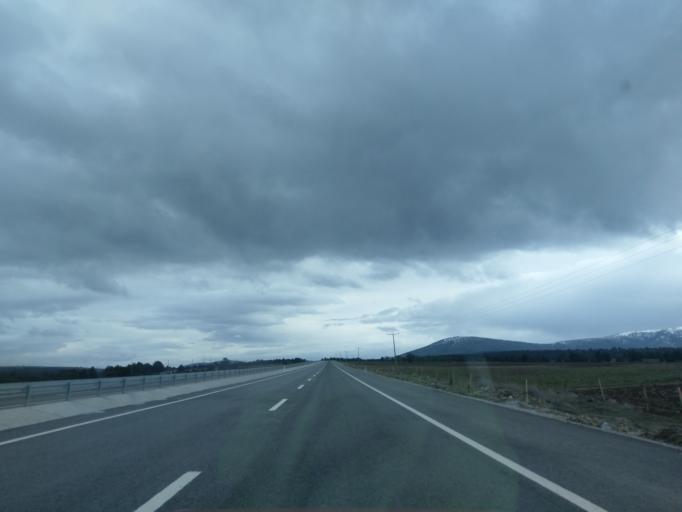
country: TR
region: Kuetahya
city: Cavdarhisar
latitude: 39.2249
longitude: 29.7234
